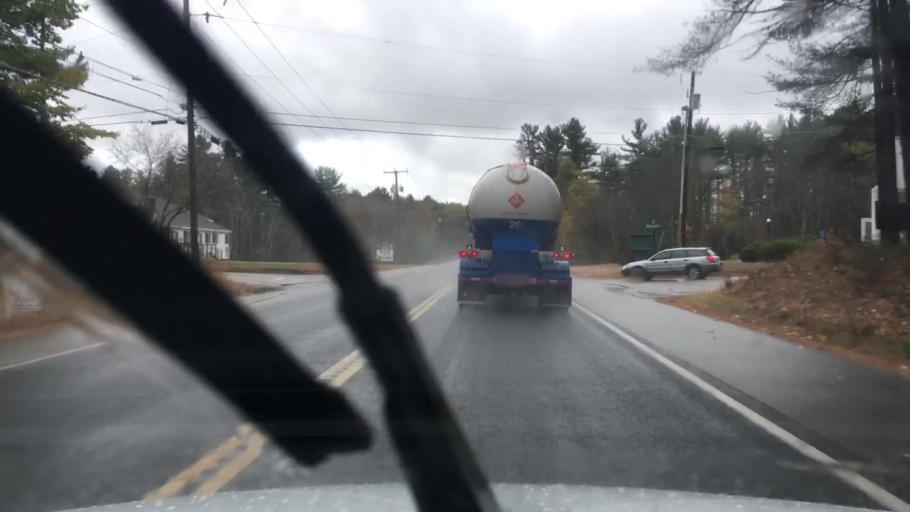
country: US
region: New Hampshire
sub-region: Strafford County
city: Barrington
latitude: 43.2012
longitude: -70.9973
